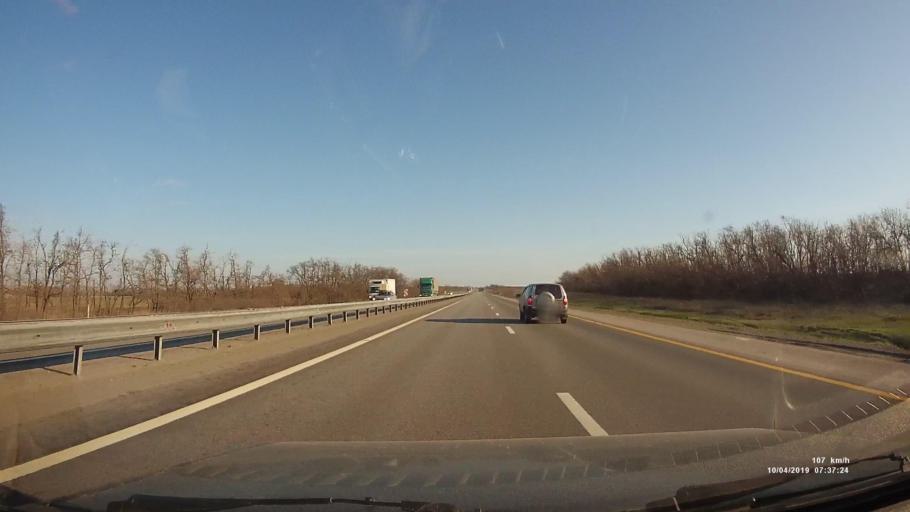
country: RU
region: Rostov
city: Likhoy
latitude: 48.0725
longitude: 40.2595
